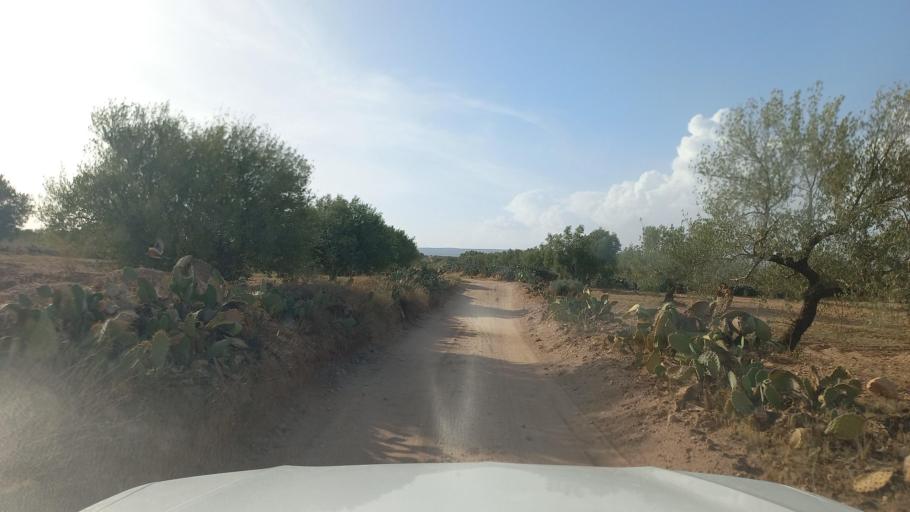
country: TN
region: Al Qasrayn
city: Kasserine
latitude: 35.2303
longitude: 8.9260
